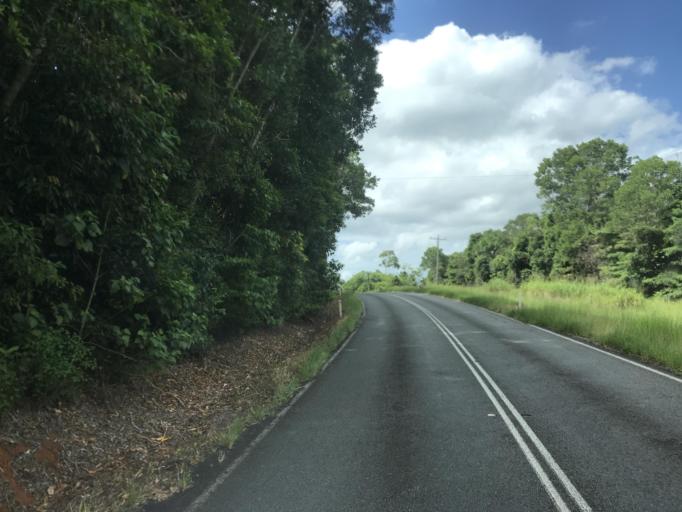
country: AU
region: Queensland
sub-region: Cassowary Coast
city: Innisfail
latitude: -17.8359
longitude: 146.0524
